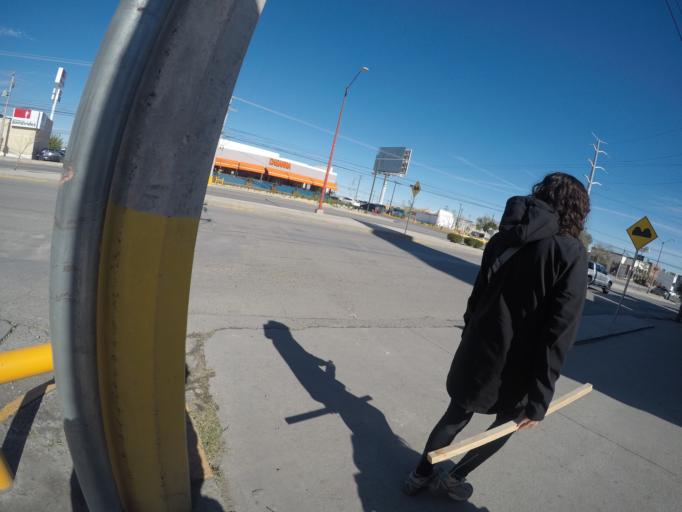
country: MX
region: Chihuahua
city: Ciudad Juarez
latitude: 31.7322
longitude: -106.4130
